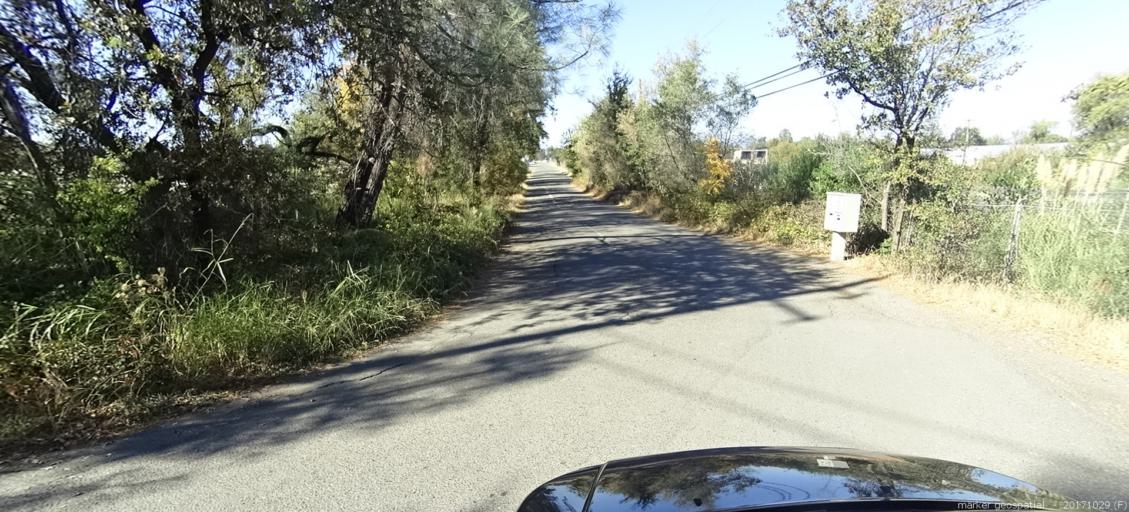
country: US
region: California
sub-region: Shasta County
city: Anderson
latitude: 40.4846
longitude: -122.3519
